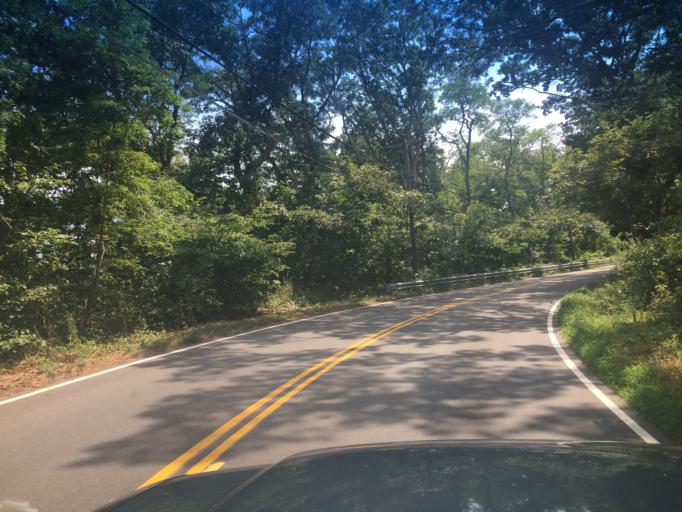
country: US
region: Massachusetts
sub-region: Barnstable County
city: Falmouth
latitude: 41.5758
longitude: -70.6272
